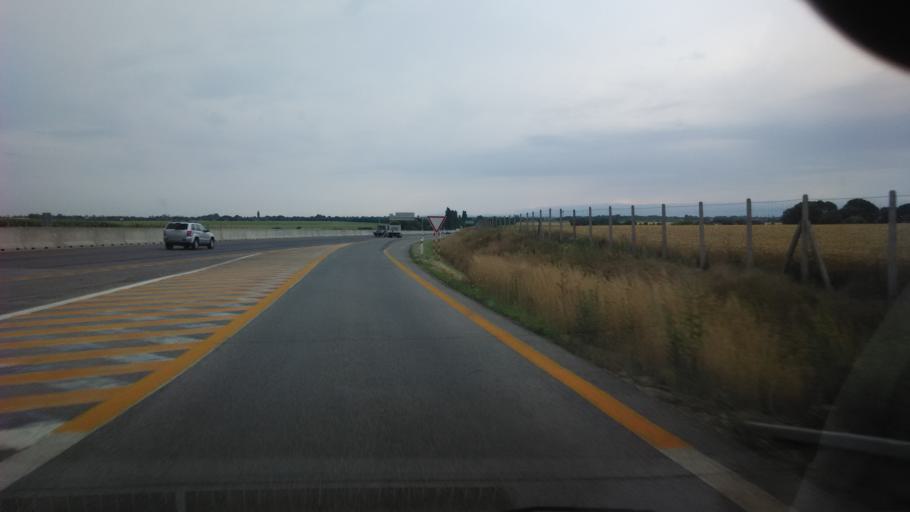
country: SK
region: Trnavsky
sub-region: Okres Trnava
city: Trnava
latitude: 48.3077
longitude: 17.5565
